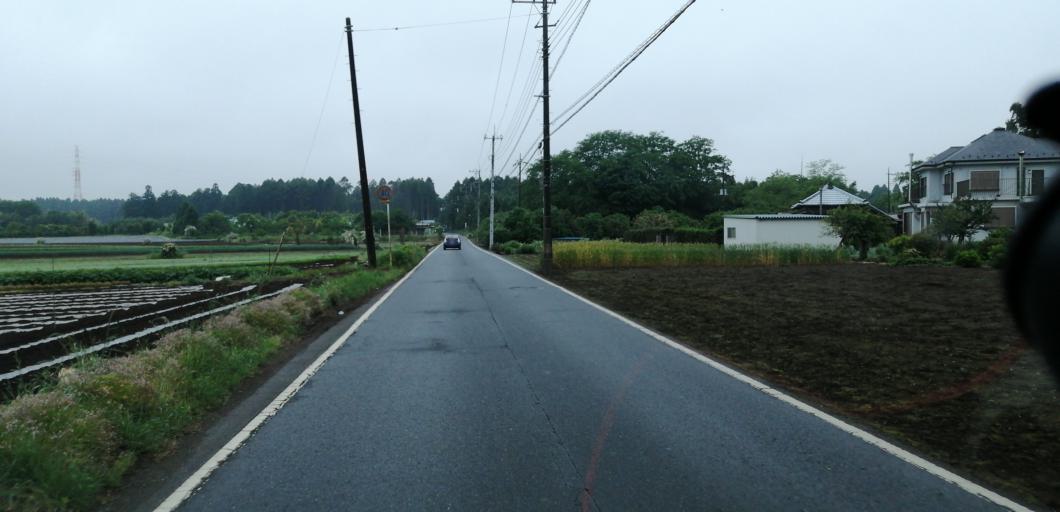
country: JP
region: Chiba
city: Oami
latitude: 35.5686
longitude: 140.2610
